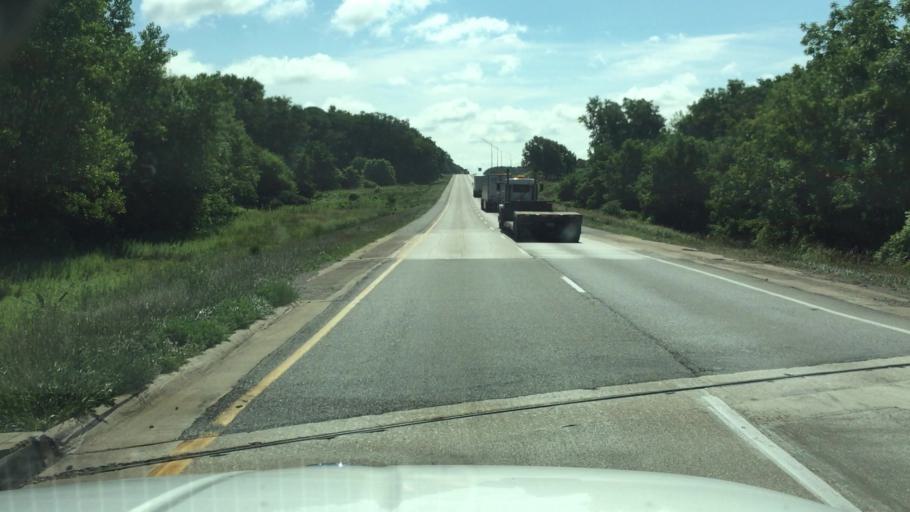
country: US
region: Iowa
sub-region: Muscatine County
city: Wilton
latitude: 41.6417
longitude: -91.0630
